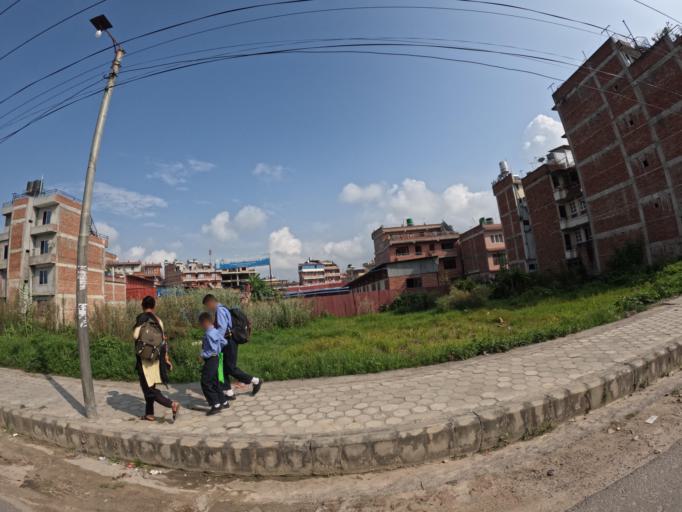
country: NP
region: Central Region
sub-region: Bagmati Zone
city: Bhaktapur
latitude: 27.6790
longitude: 85.4437
